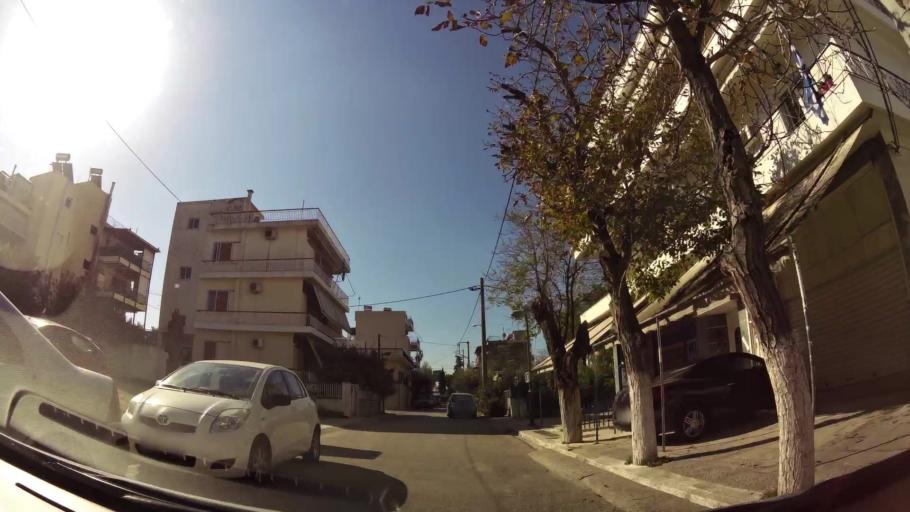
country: GR
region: Attica
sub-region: Nomarchia Athinas
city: Metamorfosi
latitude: 38.0670
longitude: 23.7536
